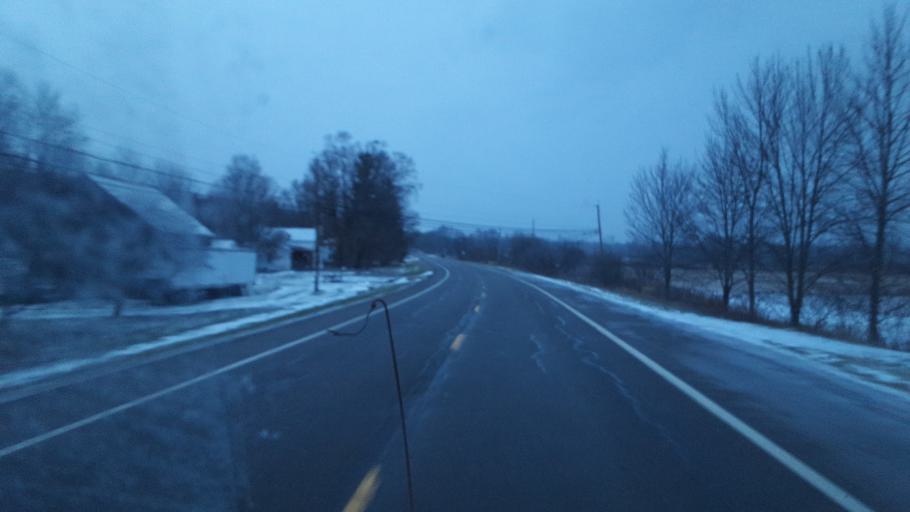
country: US
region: New York
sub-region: Allegany County
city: Belmont
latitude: 42.2395
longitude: -78.0527
